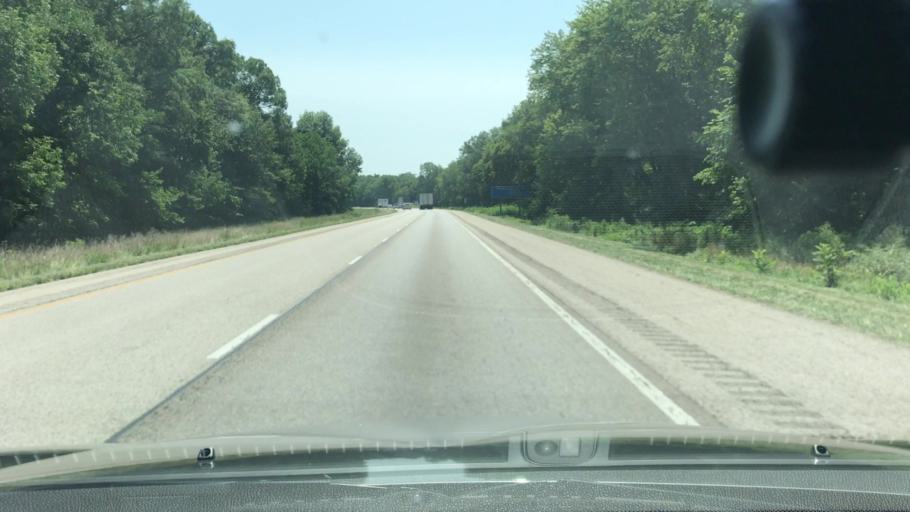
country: US
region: Illinois
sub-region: Washington County
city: Nashville
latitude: 38.4037
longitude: -89.4055
